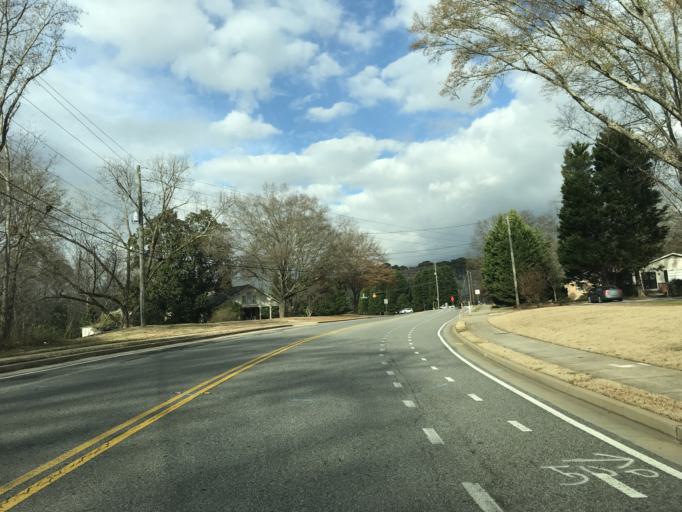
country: US
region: Georgia
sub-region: Fulton County
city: Alpharetta
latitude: 34.0866
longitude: -84.3065
